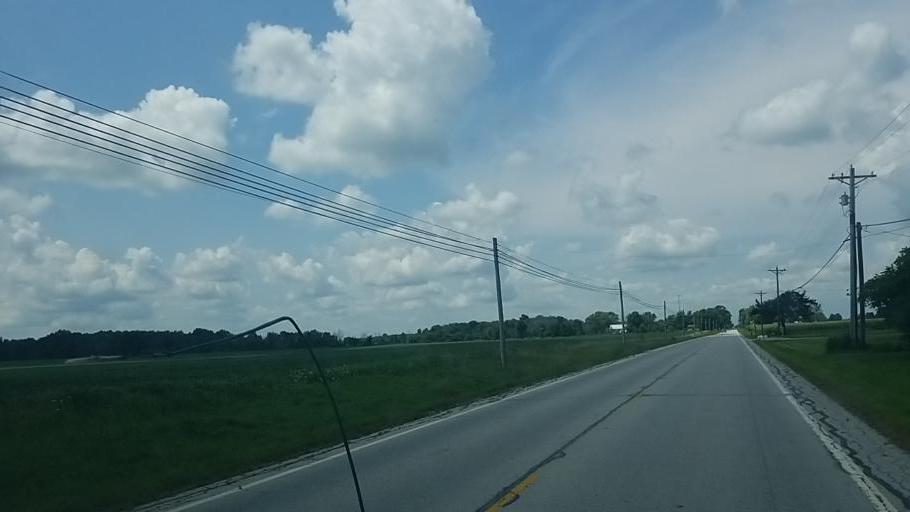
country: US
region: Ohio
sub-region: Wayne County
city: West Salem
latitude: 41.0270
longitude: -82.1063
